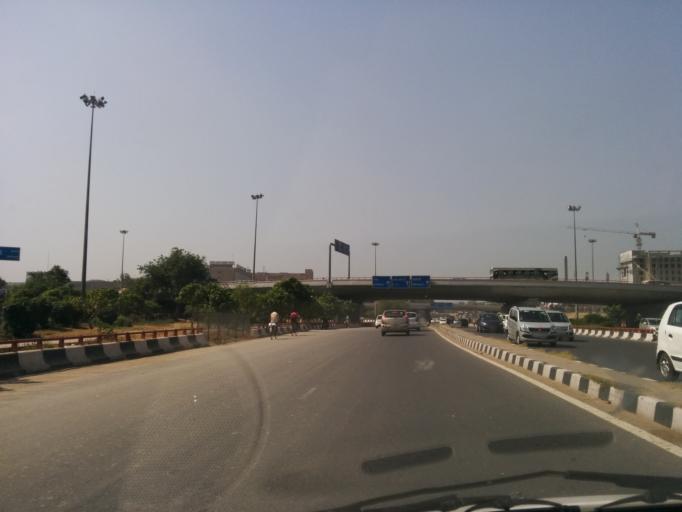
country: IN
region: NCT
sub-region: New Delhi
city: New Delhi
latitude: 28.5717
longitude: 77.2092
